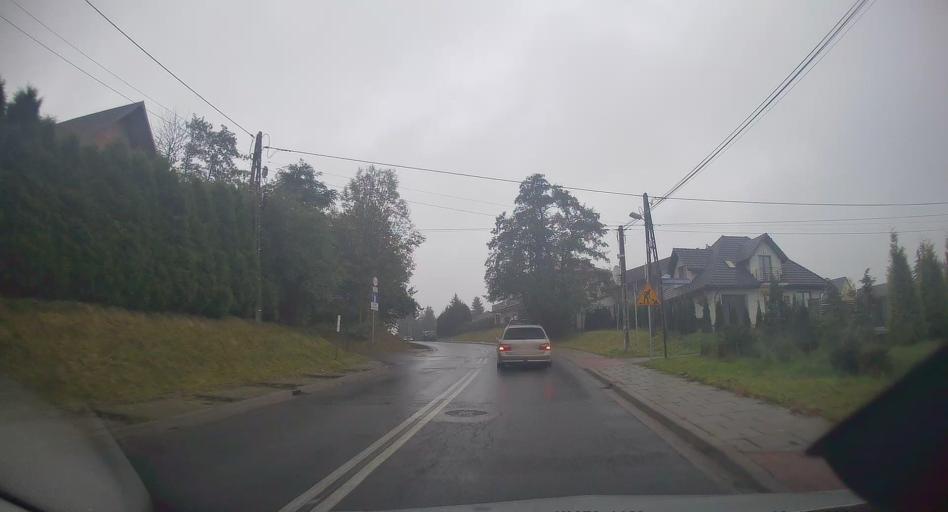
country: PL
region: Lesser Poland Voivodeship
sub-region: Powiat krakowski
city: Ochojno
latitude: 49.9765
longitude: 19.9864
